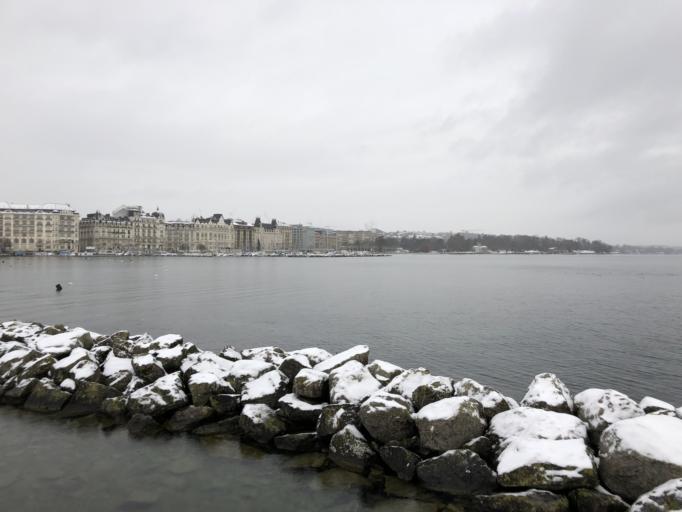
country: CH
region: Geneva
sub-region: Geneva
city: Geneve
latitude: 46.2100
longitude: 6.1569
